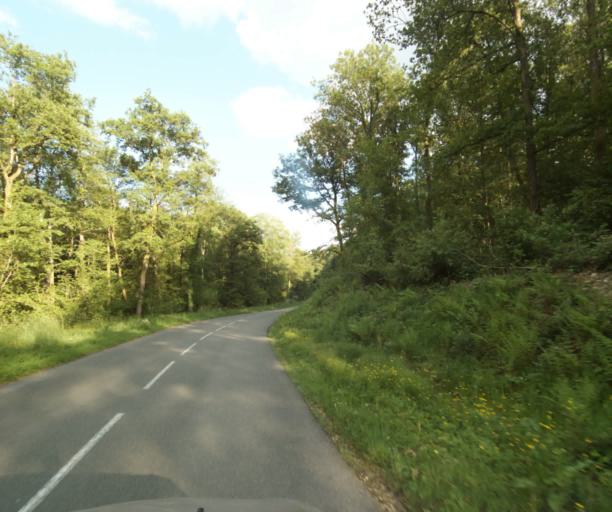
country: FR
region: Champagne-Ardenne
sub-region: Departement des Ardennes
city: Nouzonville
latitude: 49.8263
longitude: 4.7070
